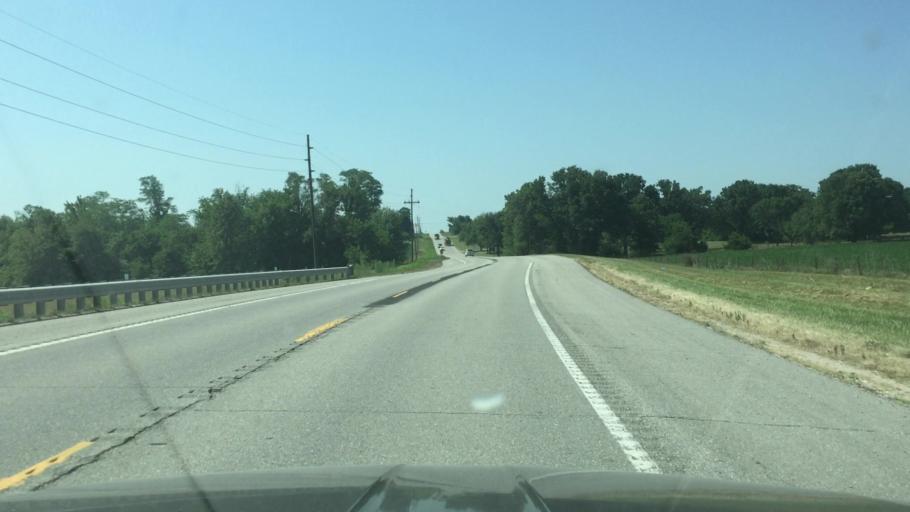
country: US
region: Missouri
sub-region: Moniteau County
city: Tipton
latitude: 38.6300
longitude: -92.7893
